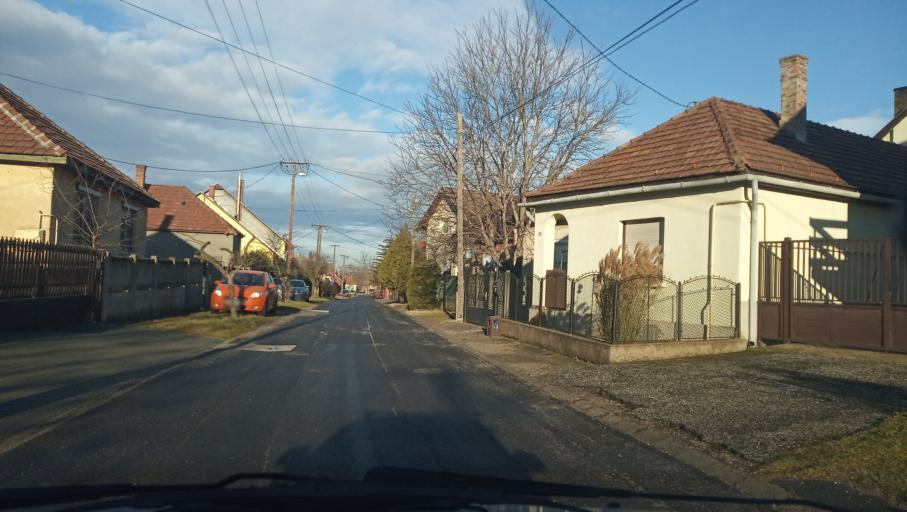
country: HU
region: Komarom-Esztergom
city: Piliscsev
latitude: 47.6716
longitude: 18.8209
